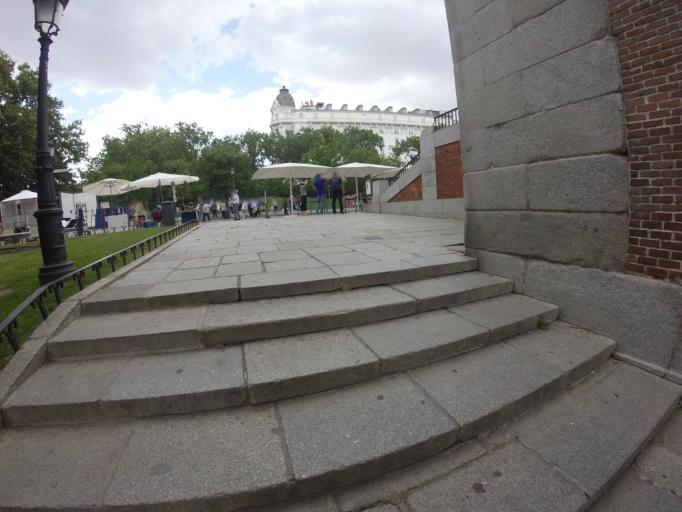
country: ES
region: Madrid
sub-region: Provincia de Madrid
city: Retiro
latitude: 40.4146
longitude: -3.6928
